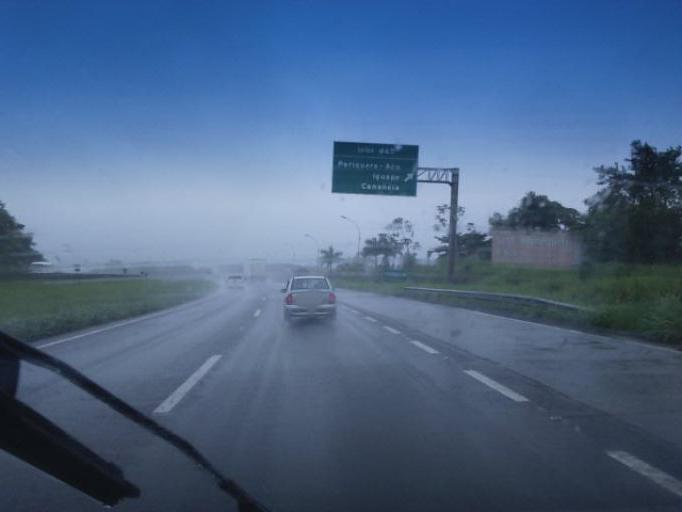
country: BR
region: Sao Paulo
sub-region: Pariquera-Acu
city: Pariquera Acu
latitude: -24.6476
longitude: -47.9224
